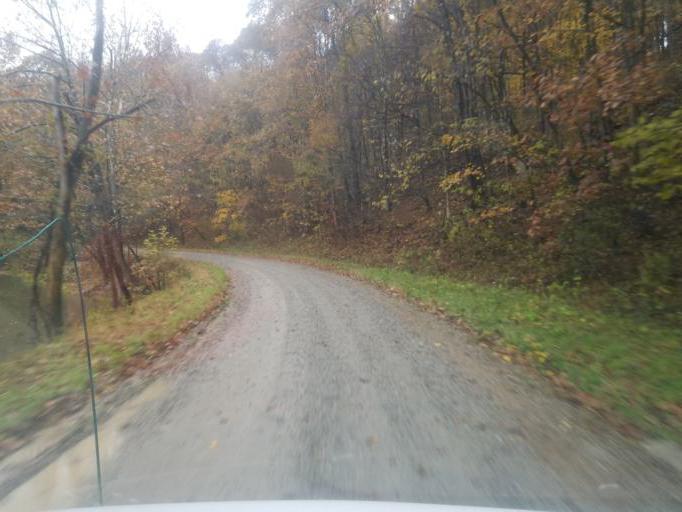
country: US
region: Ohio
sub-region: Washington County
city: Beverly
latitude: 39.4808
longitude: -81.7389
